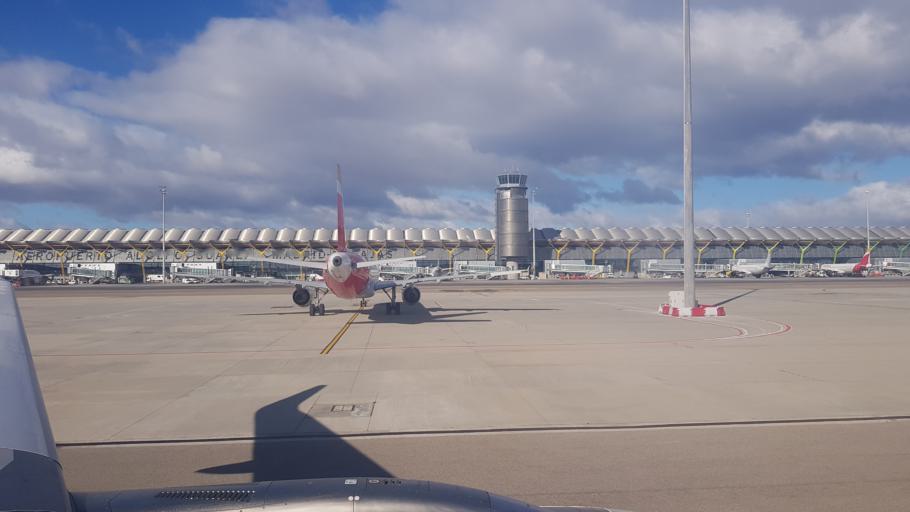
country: ES
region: Madrid
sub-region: Provincia de Madrid
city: Barajas de Madrid
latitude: 40.4917
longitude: -3.5865
